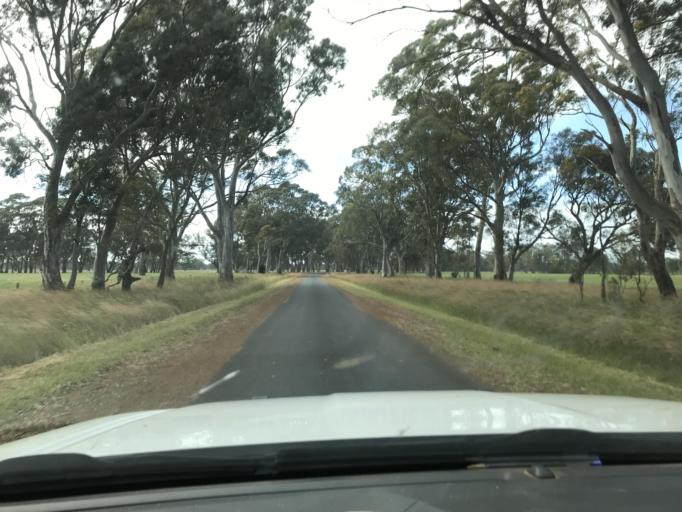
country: AU
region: South Australia
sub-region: Wattle Range
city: Penola
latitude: -37.1788
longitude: 141.2776
